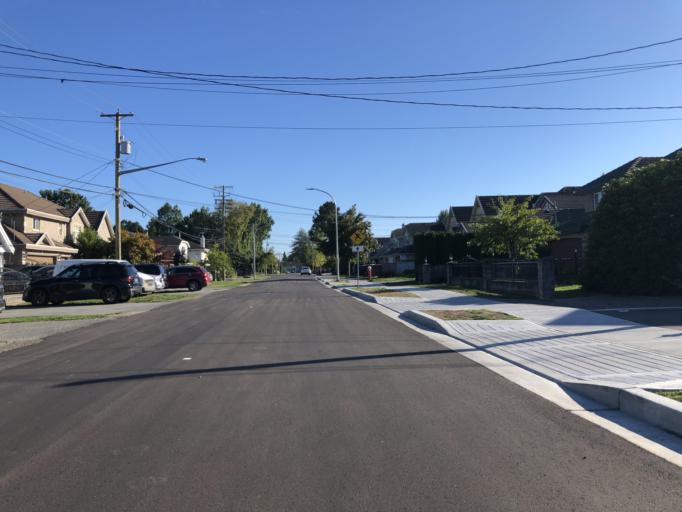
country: CA
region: British Columbia
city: Richmond
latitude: 49.1512
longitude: -123.1225
